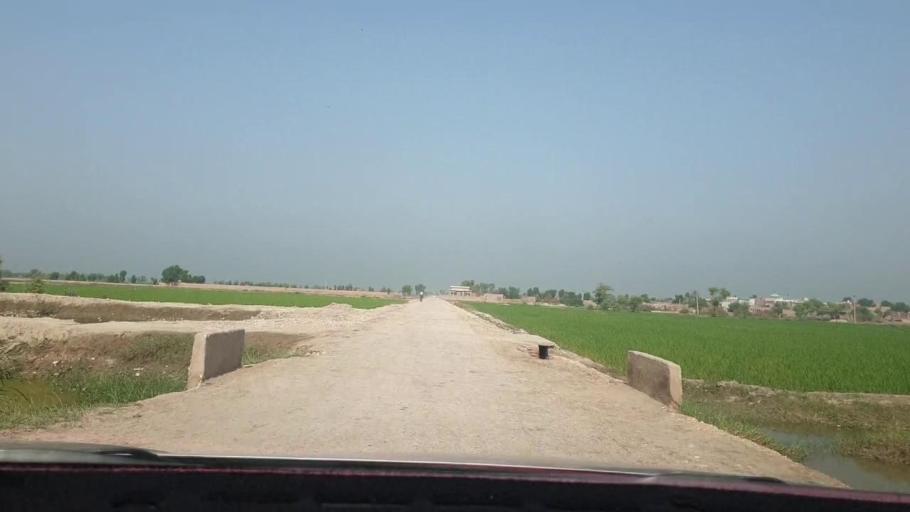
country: PK
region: Sindh
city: Nasirabad
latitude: 27.4357
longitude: 67.9604
